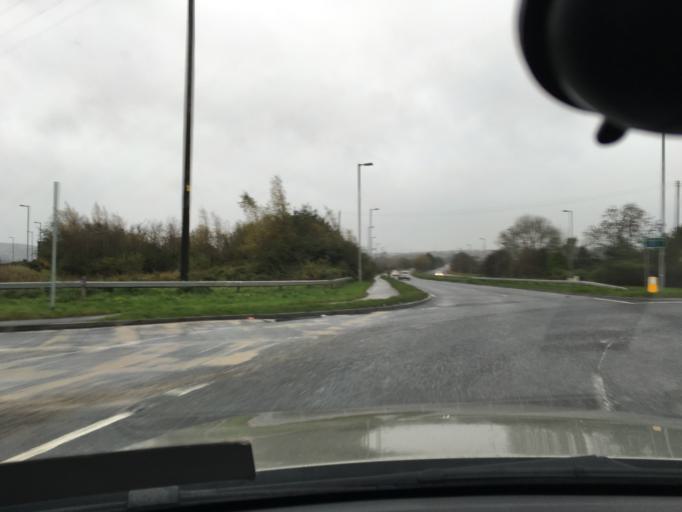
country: GB
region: Northern Ireland
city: Carnmoney
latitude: 54.7048
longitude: -5.9682
